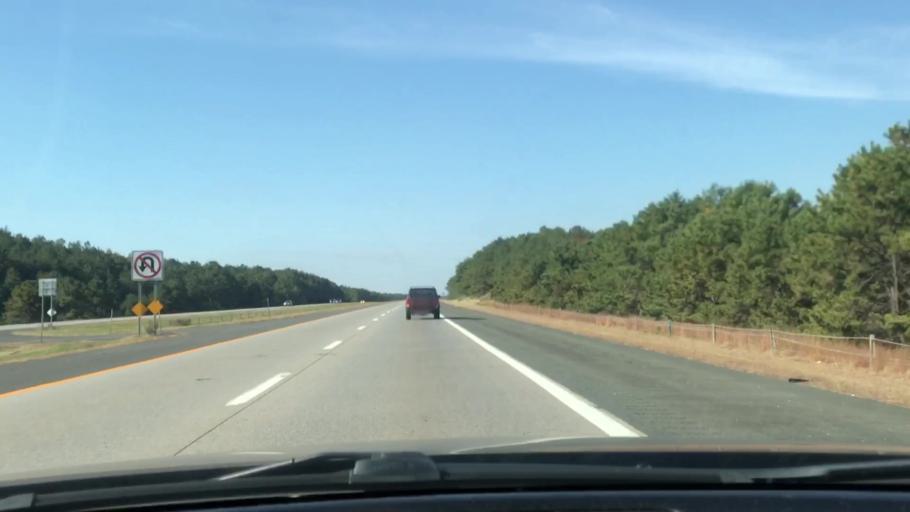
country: US
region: New York
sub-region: Suffolk County
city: East Quogue
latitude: 40.8759
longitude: -72.5713
